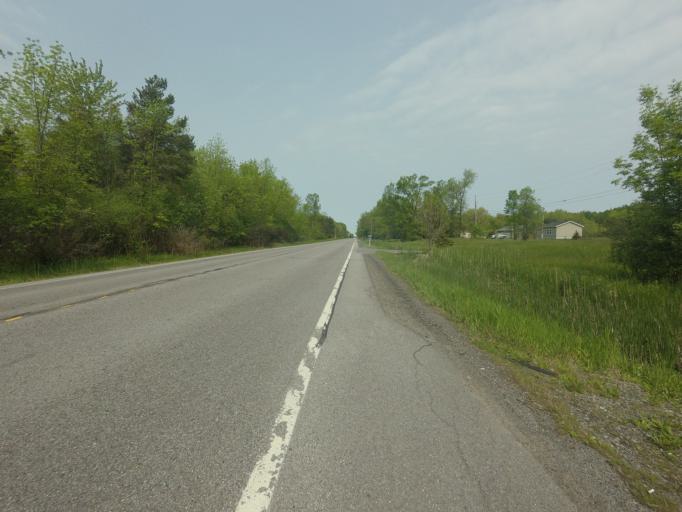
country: US
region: New York
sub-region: Jefferson County
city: Dexter
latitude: 44.0170
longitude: -76.0262
